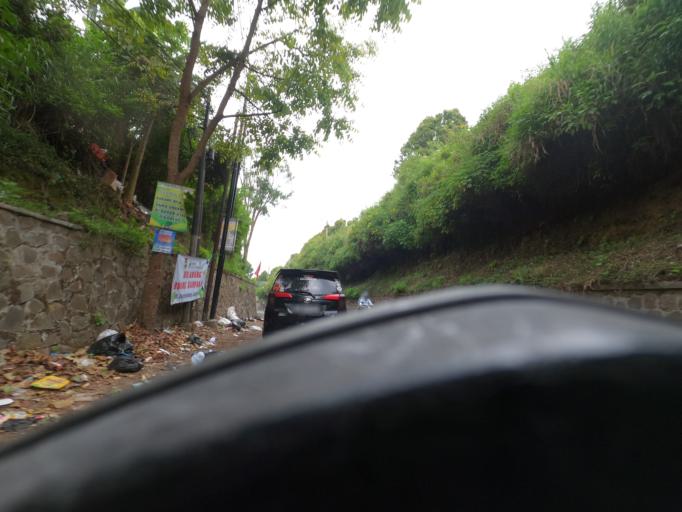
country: ID
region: West Java
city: Lembang
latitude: -6.8140
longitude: 107.5580
